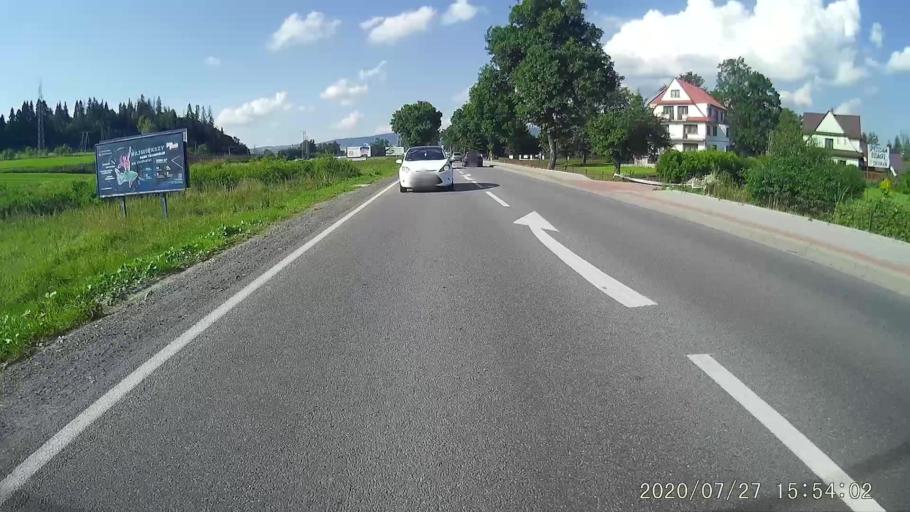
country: PL
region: Lesser Poland Voivodeship
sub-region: Powiat nowotarski
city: Szaflary
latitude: 49.4316
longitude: 20.0212
